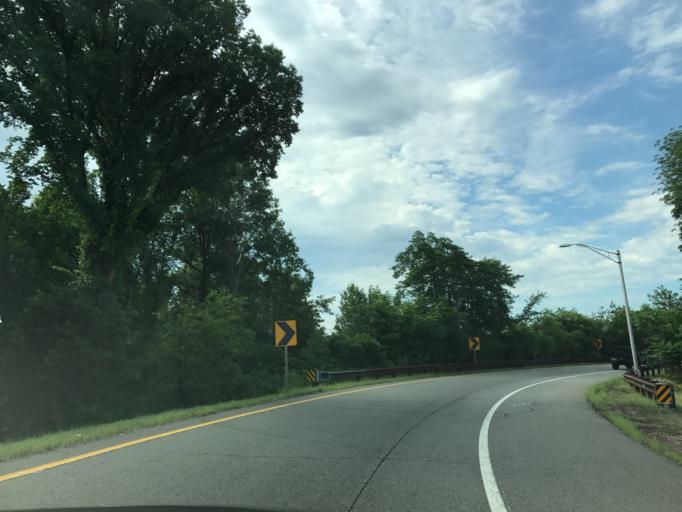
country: US
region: New Jersey
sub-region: Middlesex County
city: Iselin
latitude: 40.5530
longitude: -74.3148
